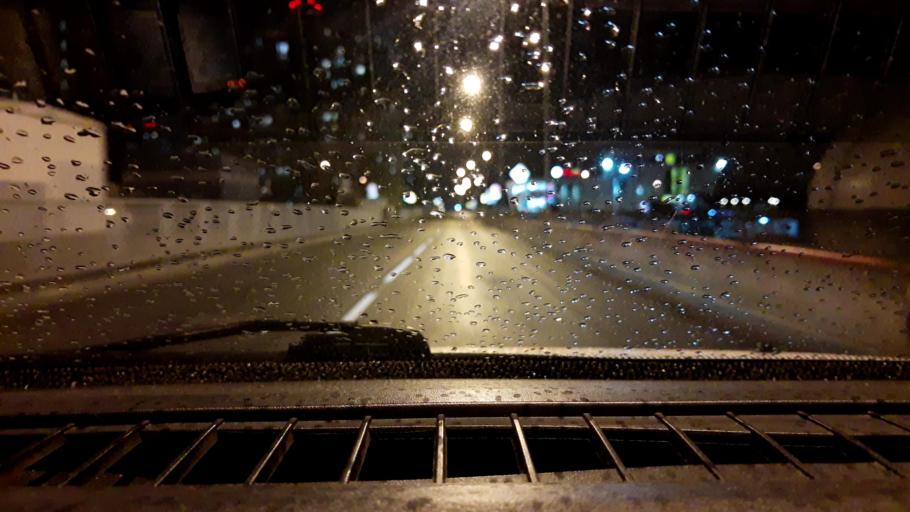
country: RU
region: Nizjnij Novgorod
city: Burevestnik
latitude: 56.2157
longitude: 43.8621
